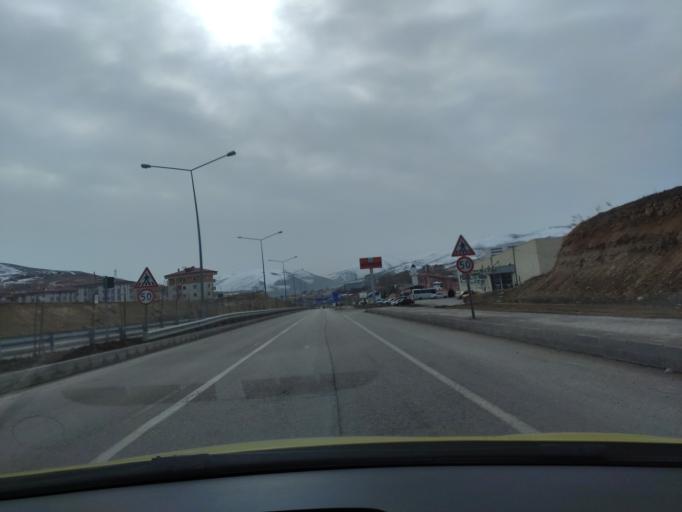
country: TR
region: Bayburt
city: Bayburt
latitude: 40.2640
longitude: 40.2059
